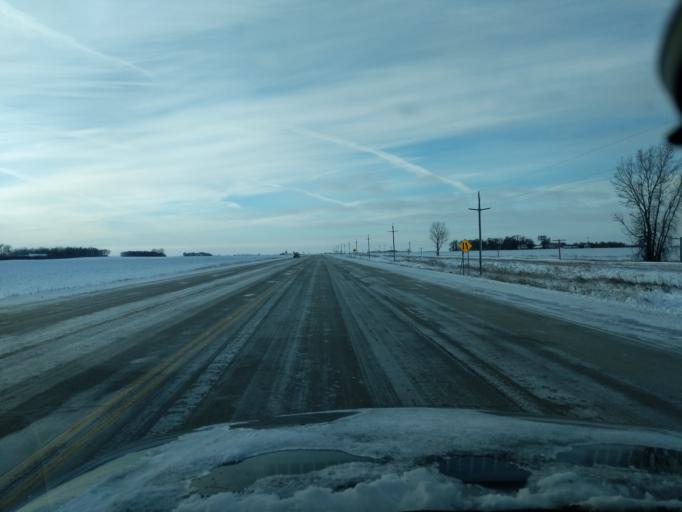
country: US
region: Minnesota
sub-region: Renville County
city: Hector
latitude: 44.7524
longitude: -94.7875
